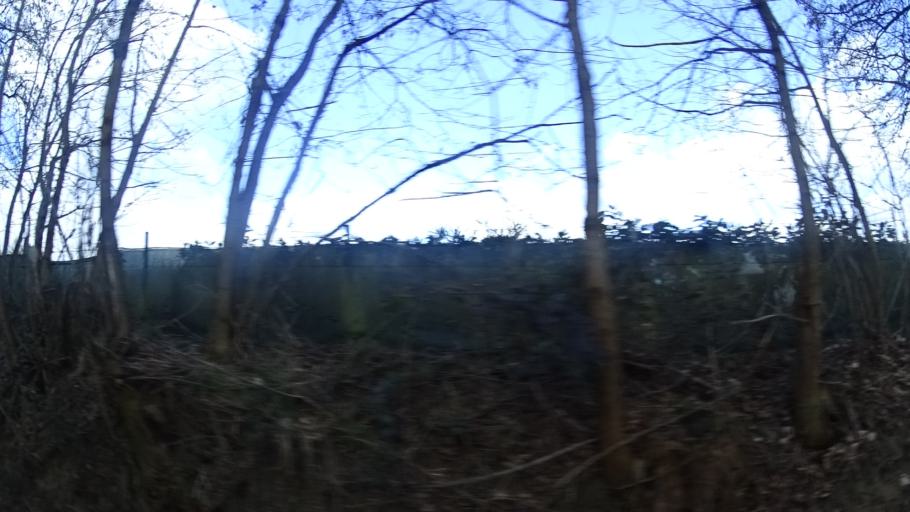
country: DE
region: Hesse
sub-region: Regierungsbezirk Darmstadt
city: Wiesbaden
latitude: 50.1014
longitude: 8.2454
